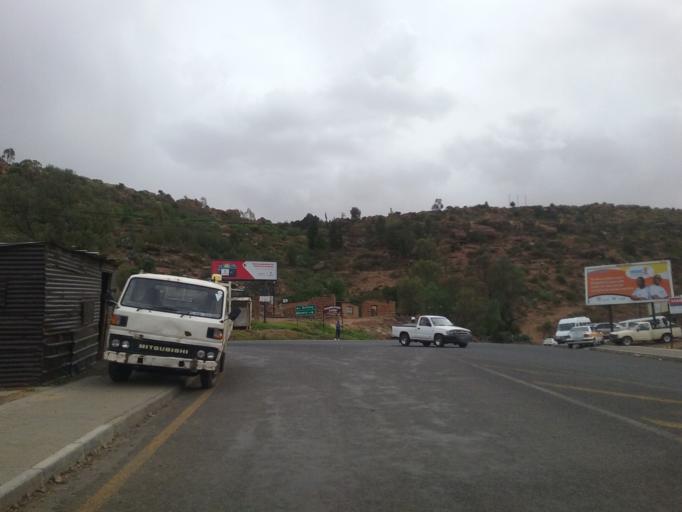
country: LS
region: Quthing
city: Quthing
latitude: -30.3981
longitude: 27.6910
